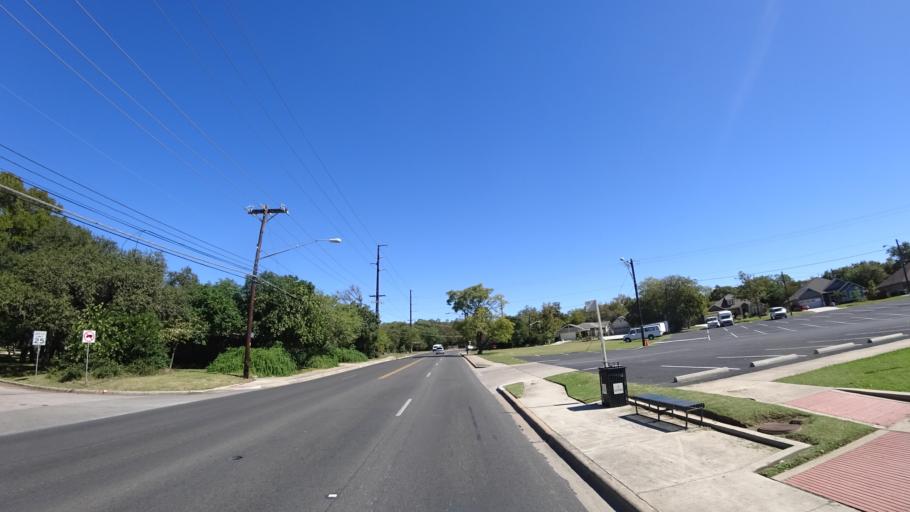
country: US
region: Texas
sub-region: Travis County
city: West Lake Hills
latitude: 30.3353
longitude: -97.7472
